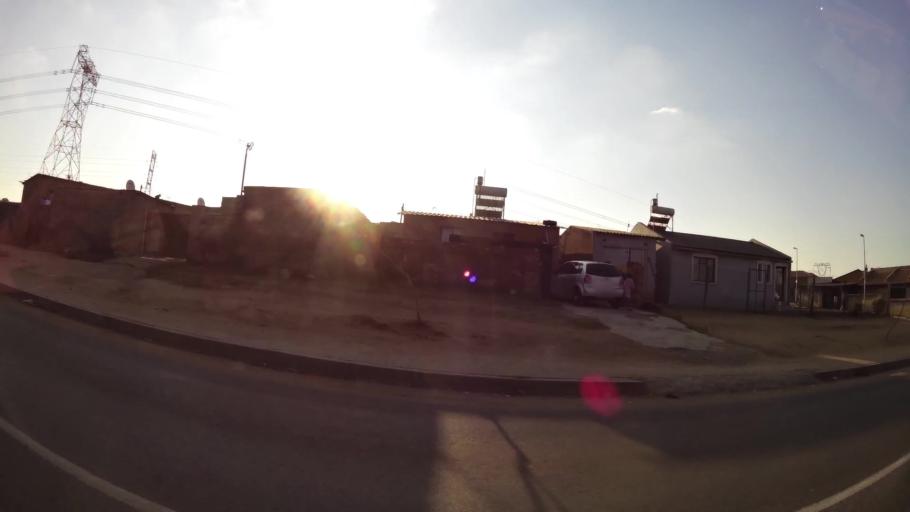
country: ZA
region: Gauteng
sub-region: Ekurhuleni Metropolitan Municipality
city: Tembisa
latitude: -26.0170
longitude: 28.1819
